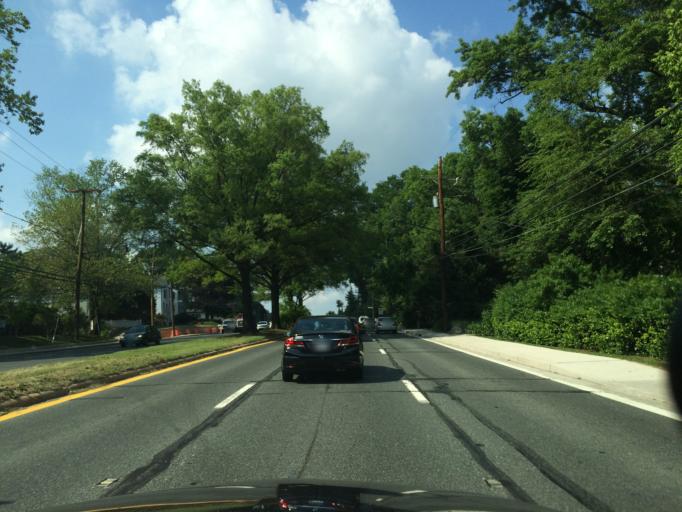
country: US
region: Maryland
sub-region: Montgomery County
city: South Kensington
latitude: 39.0184
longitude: -77.0779
